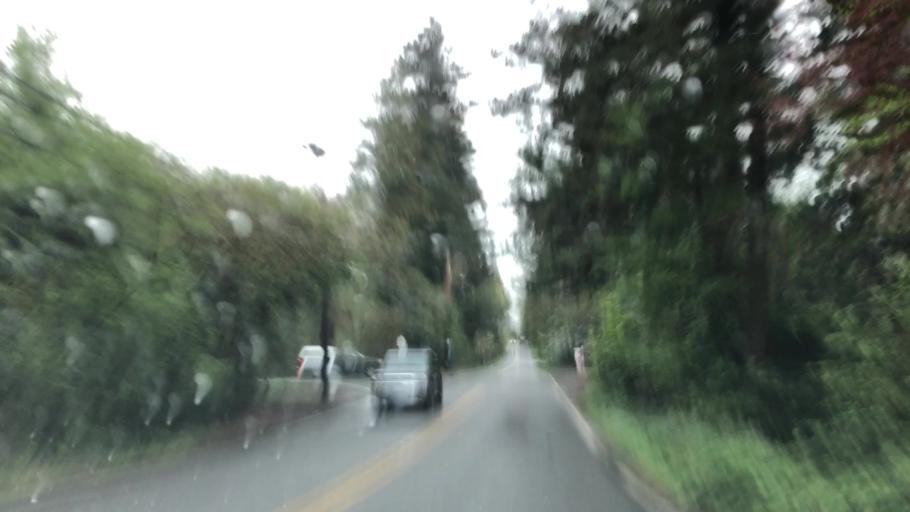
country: US
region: Oregon
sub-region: Washington County
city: Raleigh Hills
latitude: 45.4764
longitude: -122.7436
